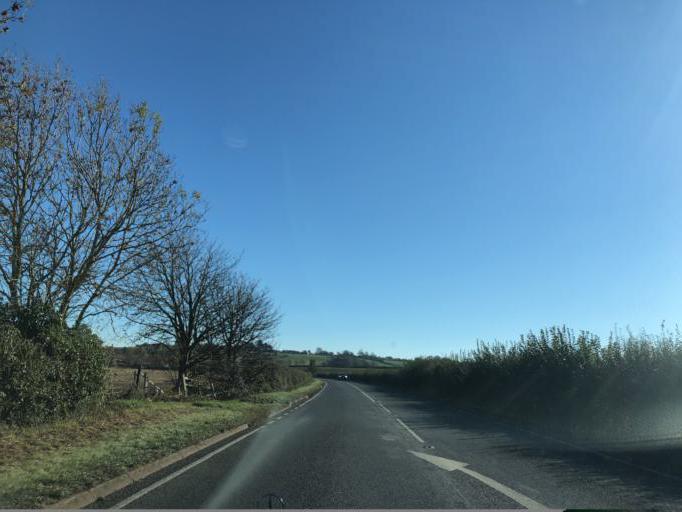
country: GB
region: England
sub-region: Warwickshire
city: Harbury
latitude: 52.2627
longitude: -1.4596
